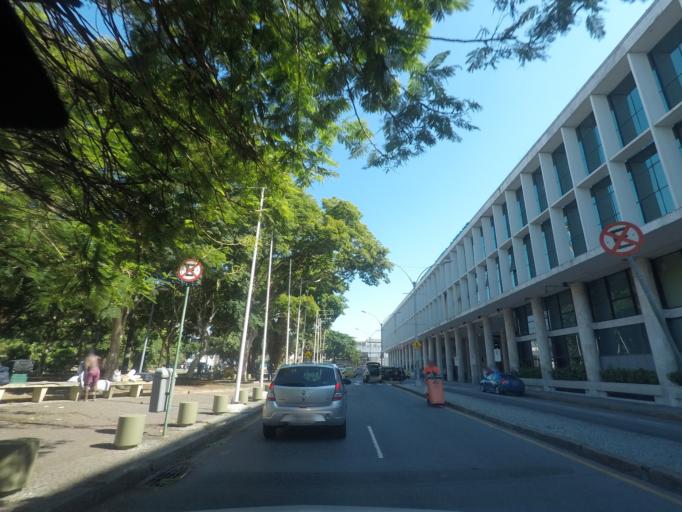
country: BR
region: Rio de Janeiro
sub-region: Rio De Janeiro
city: Rio de Janeiro
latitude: -22.9115
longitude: -43.1671
